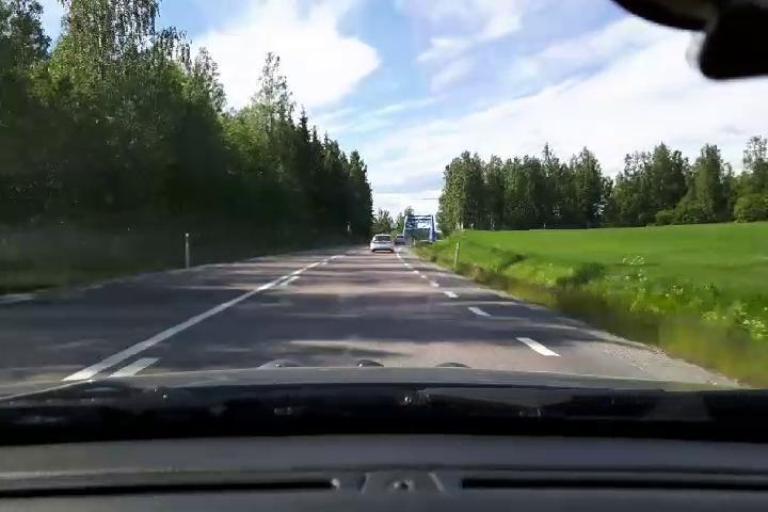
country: SE
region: Gaevleborg
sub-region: Bollnas Kommun
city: Bollnas
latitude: 61.3141
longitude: 16.4418
